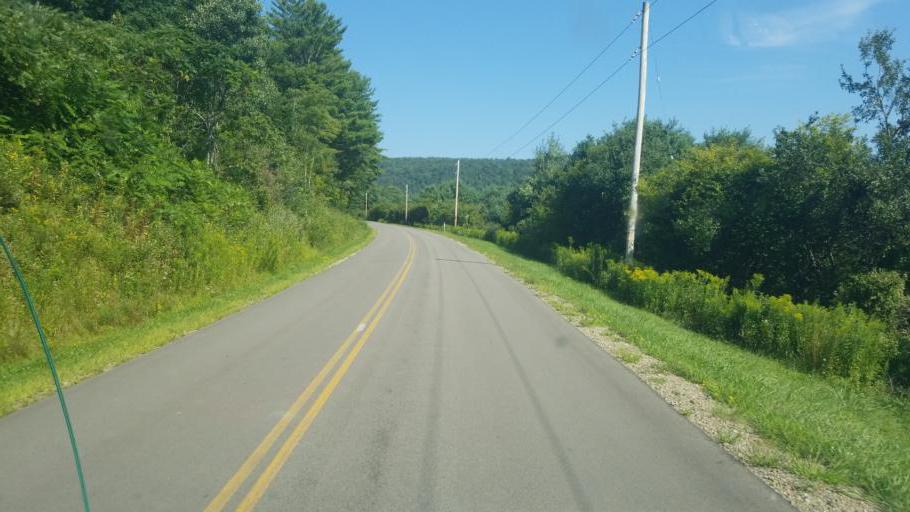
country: US
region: New York
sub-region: Allegany County
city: Bolivar
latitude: 42.0101
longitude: -78.0429
